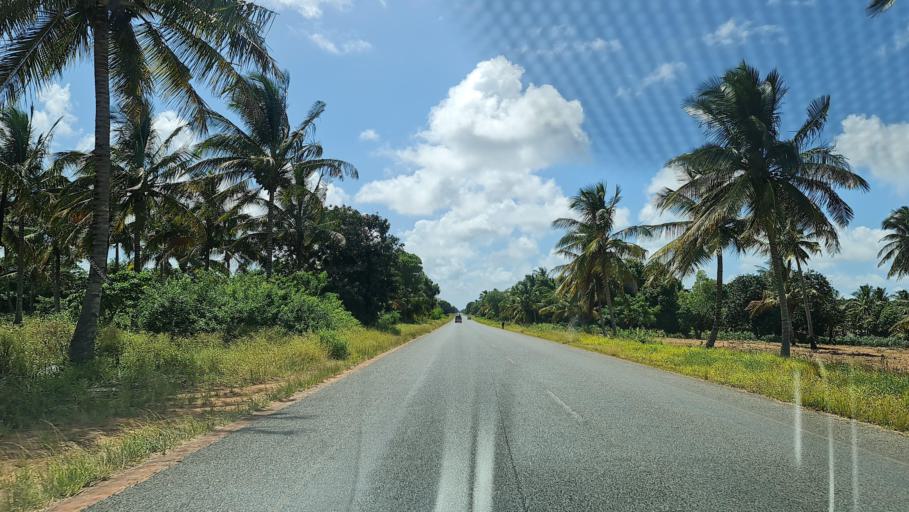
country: MZ
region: Inhambane
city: Maxixe
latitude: -24.5421
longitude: 34.9021
